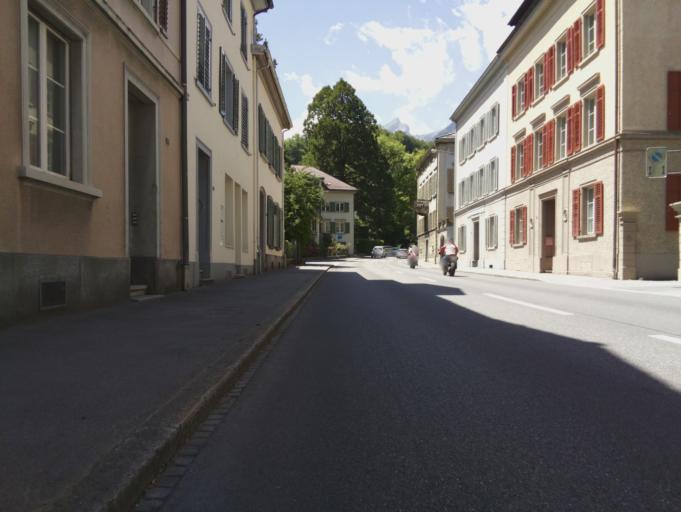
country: CH
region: Glarus
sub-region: Glarus
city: Glarus
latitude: 47.0422
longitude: 9.0657
